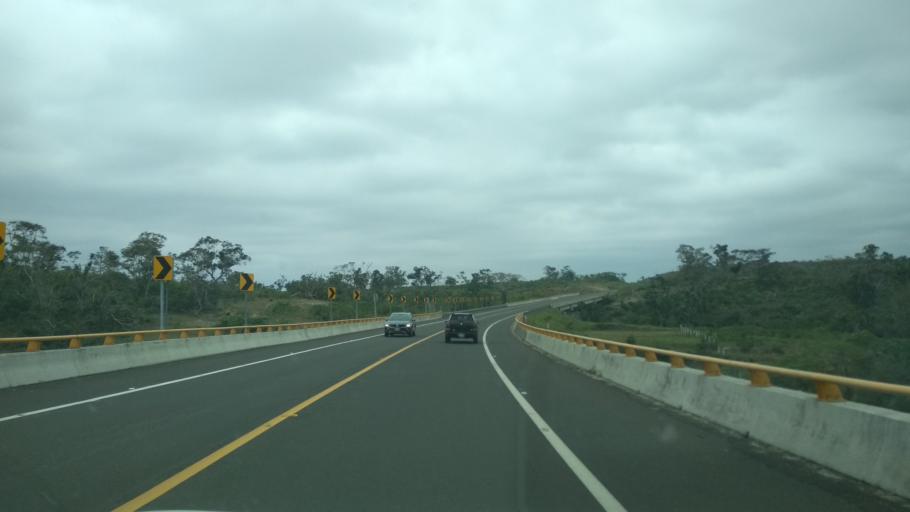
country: MX
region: Veracruz
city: Agua Dulce
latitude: 20.4260
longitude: -97.2252
